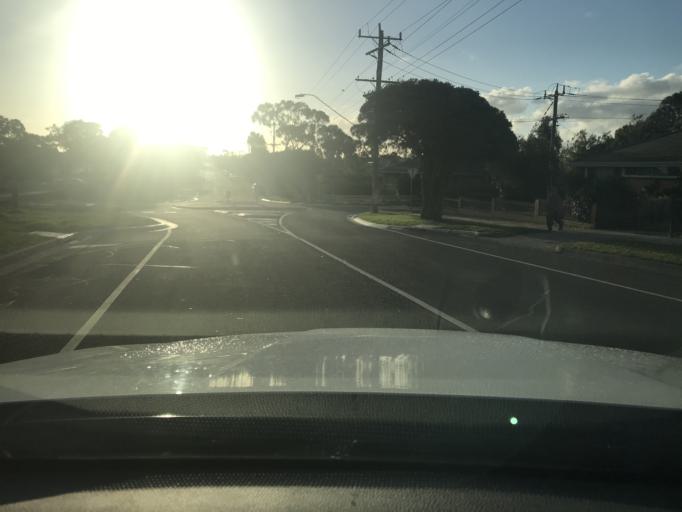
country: AU
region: Victoria
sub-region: Hume
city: Craigieburn
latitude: -37.5963
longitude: 144.9353
